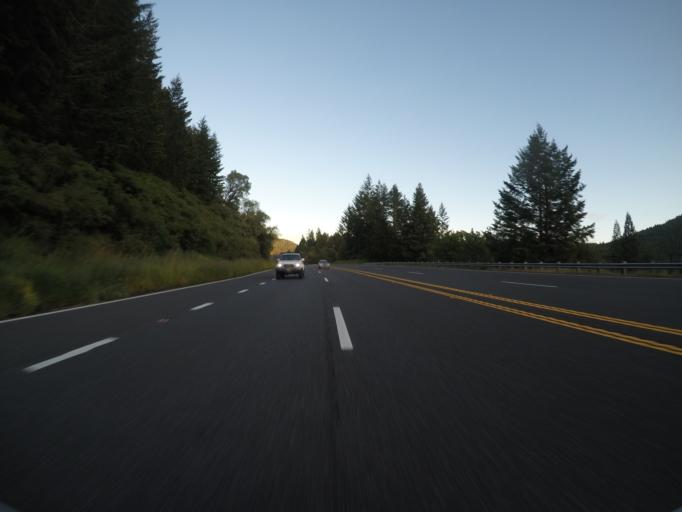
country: US
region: California
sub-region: Humboldt County
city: Redway
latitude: 39.9405
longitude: -123.7776
